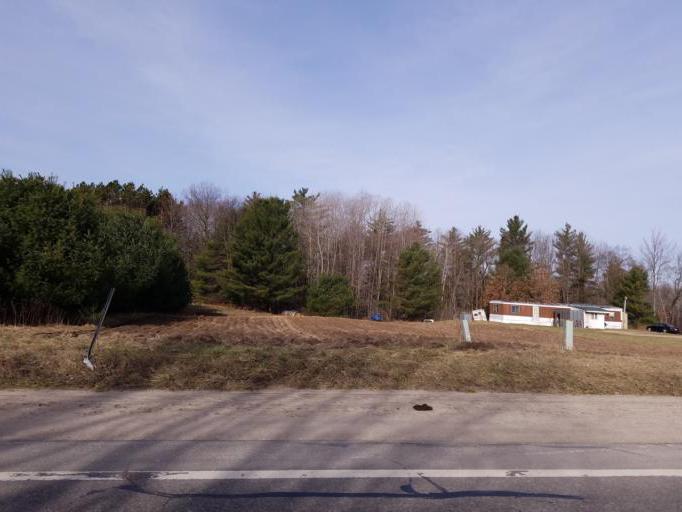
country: US
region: Michigan
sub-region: Montcalm County
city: Howard City
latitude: 43.5211
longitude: -85.4433
